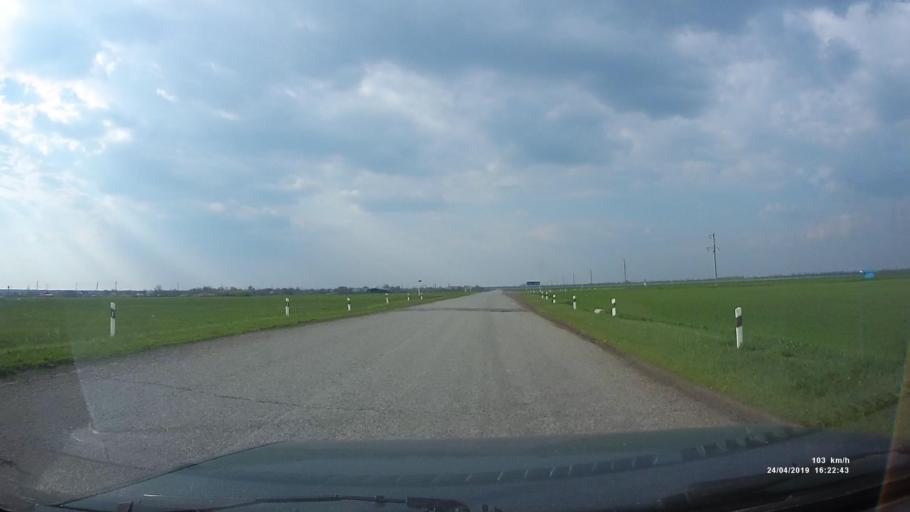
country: RU
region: Rostov
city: Orlovskiy
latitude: 46.8234
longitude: 42.0536
